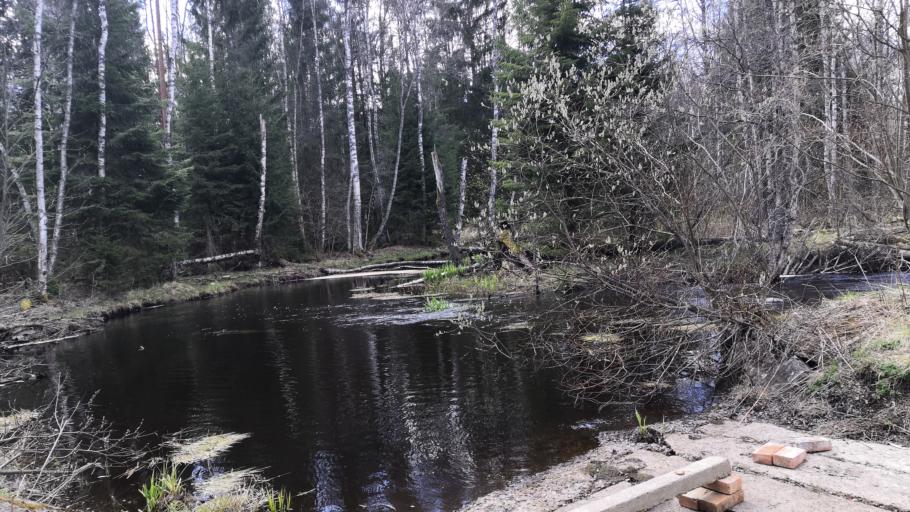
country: RU
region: Leningrad
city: Veshchevo
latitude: 60.4946
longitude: 29.2923
